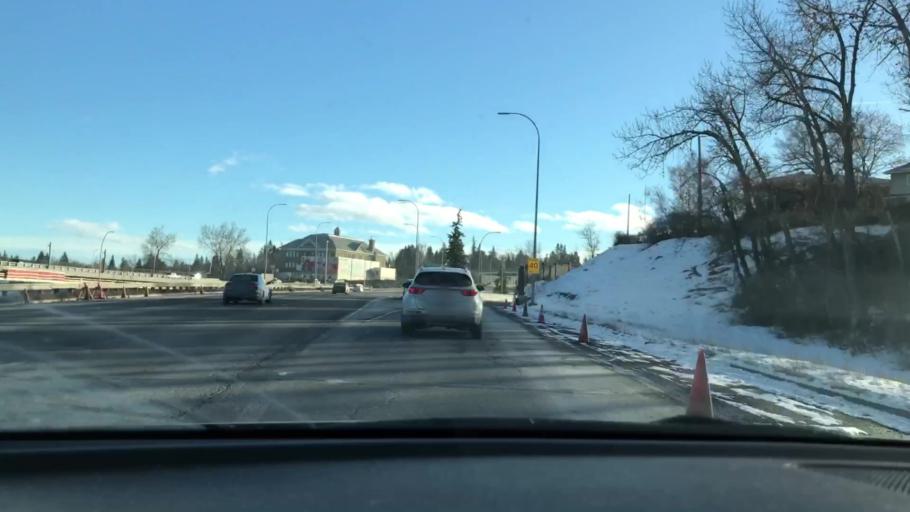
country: CA
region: Alberta
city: Calgary
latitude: 51.0444
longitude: -114.1136
